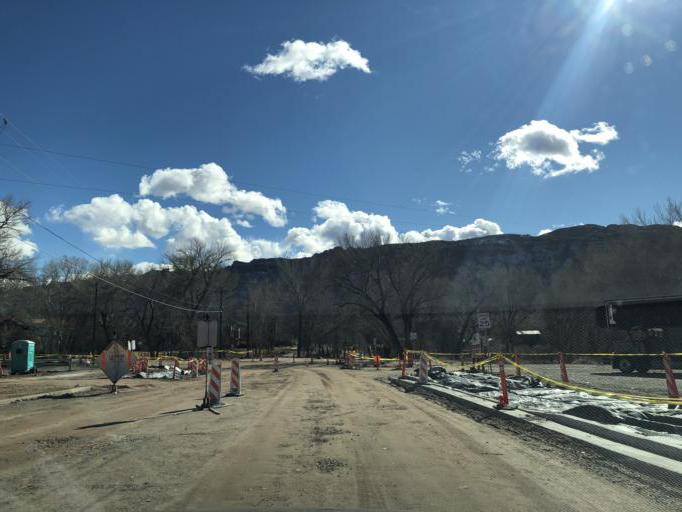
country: US
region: Utah
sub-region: Grand County
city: Moab
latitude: 38.5726
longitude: -109.5528
